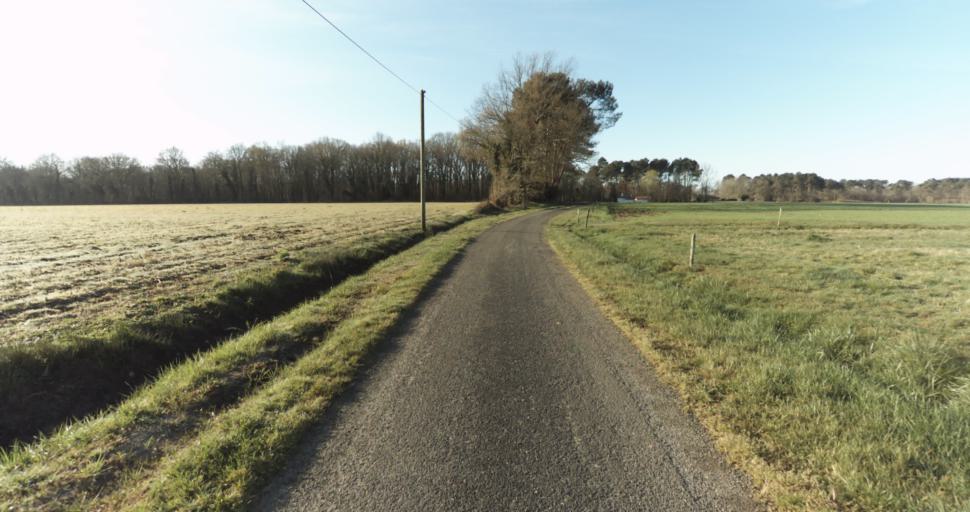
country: FR
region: Midi-Pyrenees
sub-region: Departement du Gers
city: Cazaubon
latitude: 43.9974
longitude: -0.1318
